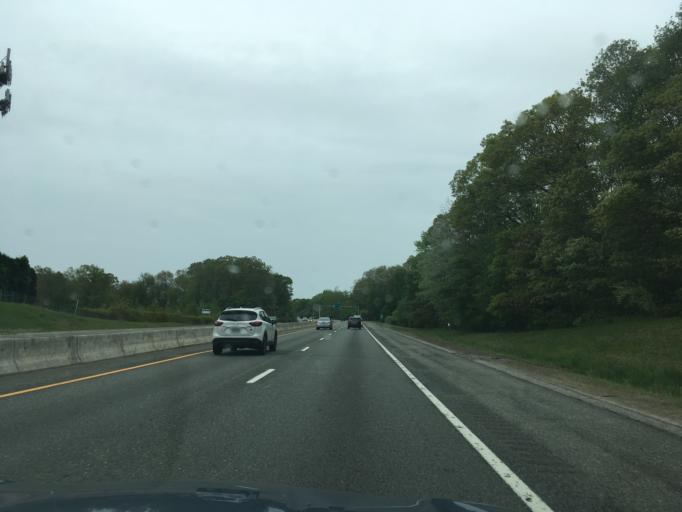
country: US
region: Rhode Island
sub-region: Washington County
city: Exeter
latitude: 41.5896
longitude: -71.5021
